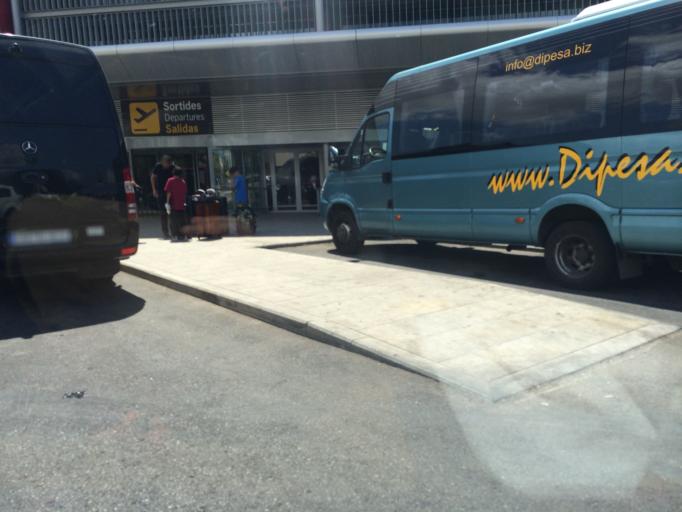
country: ES
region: Balearic Islands
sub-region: Illes Balears
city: Ibiza
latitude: 38.8759
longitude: 1.3658
